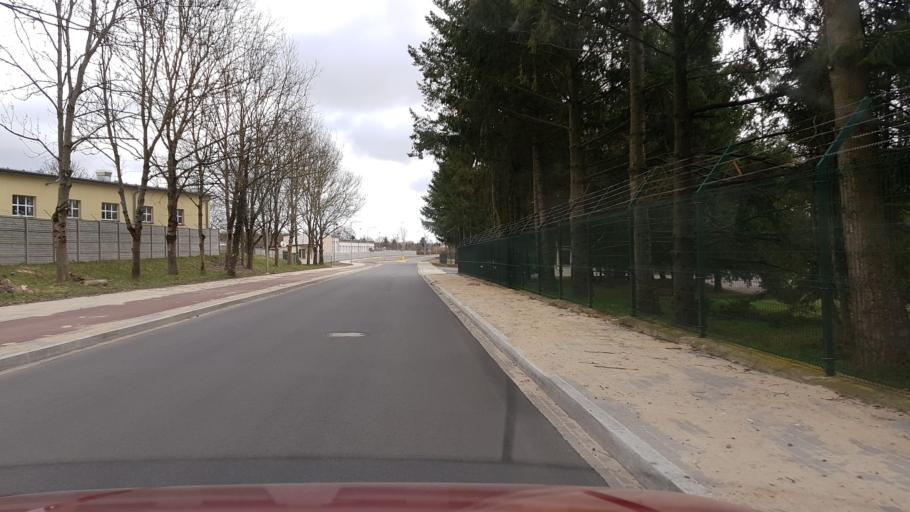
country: PL
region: West Pomeranian Voivodeship
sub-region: Koszalin
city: Koszalin
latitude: 54.1830
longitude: 16.2094
